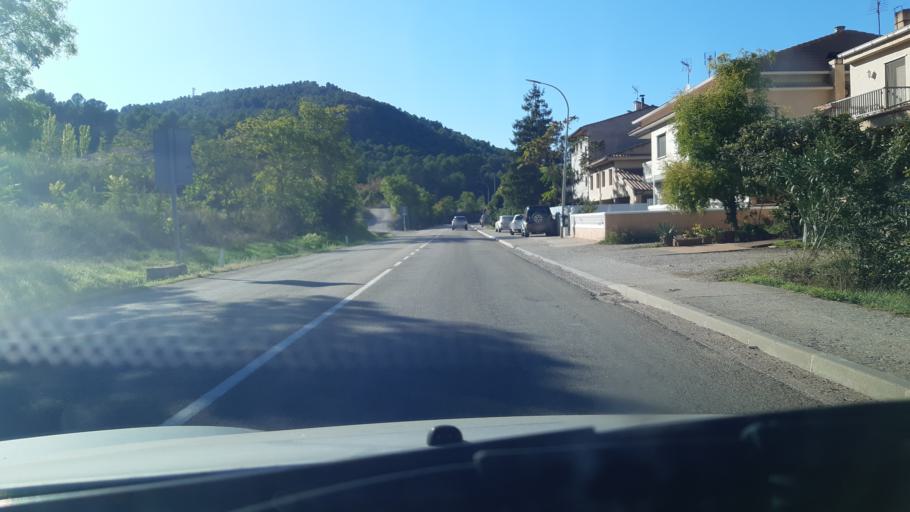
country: ES
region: Aragon
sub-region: Provincia de Teruel
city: Valderrobres
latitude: 40.8724
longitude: 0.1482
